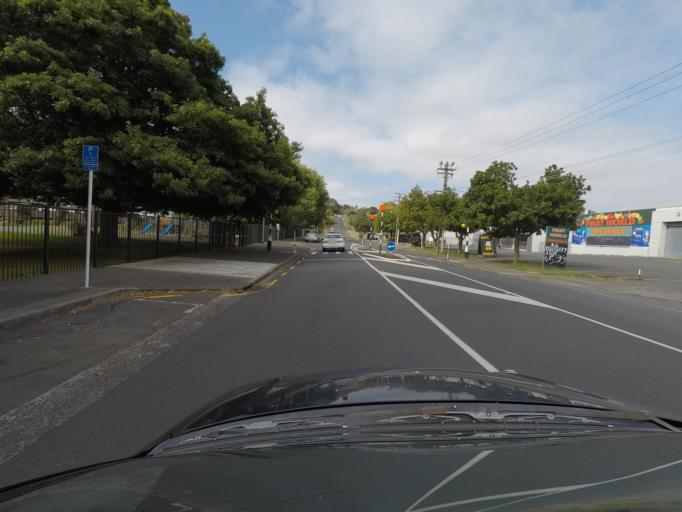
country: NZ
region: Auckland
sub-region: Auckland
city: Auckland
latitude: -36.9114
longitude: 174.7488
